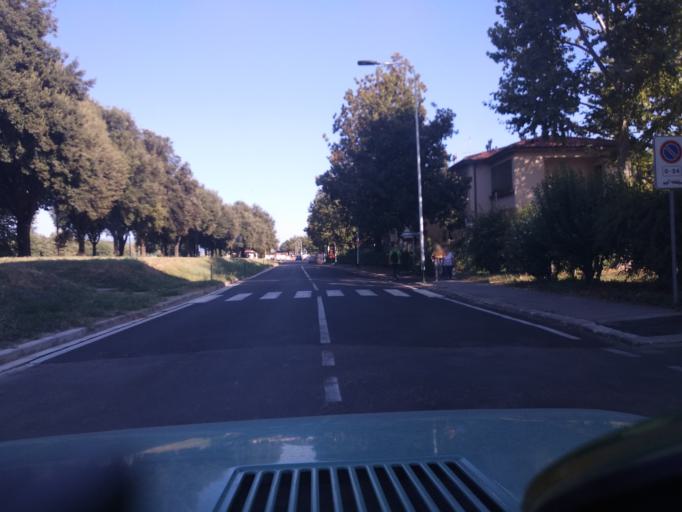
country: IT
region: Tuscany
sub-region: Province of Florence
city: Florence
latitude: 43.7802
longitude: 11.2156
